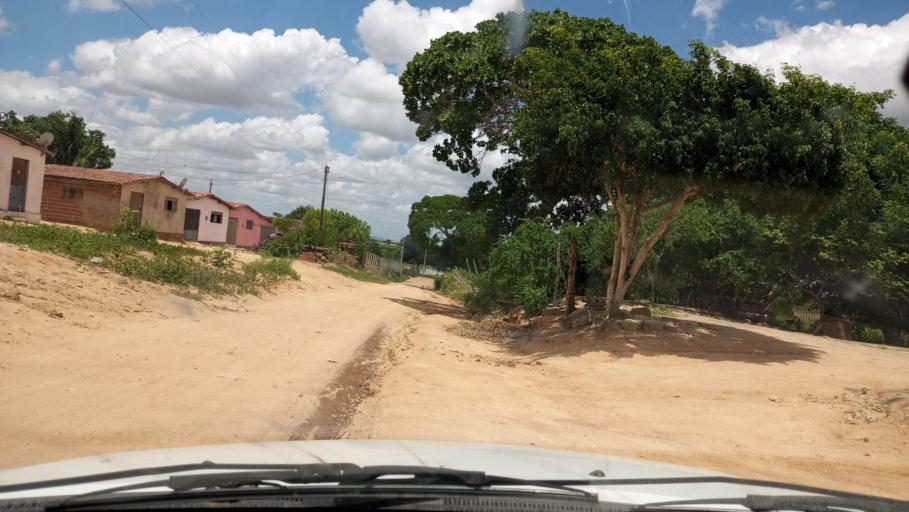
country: BR
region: Rio Grande do Norte
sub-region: Sao Jose Do Campestre
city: Sao Jose do Campestre
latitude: -6.4290
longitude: -35.6300
